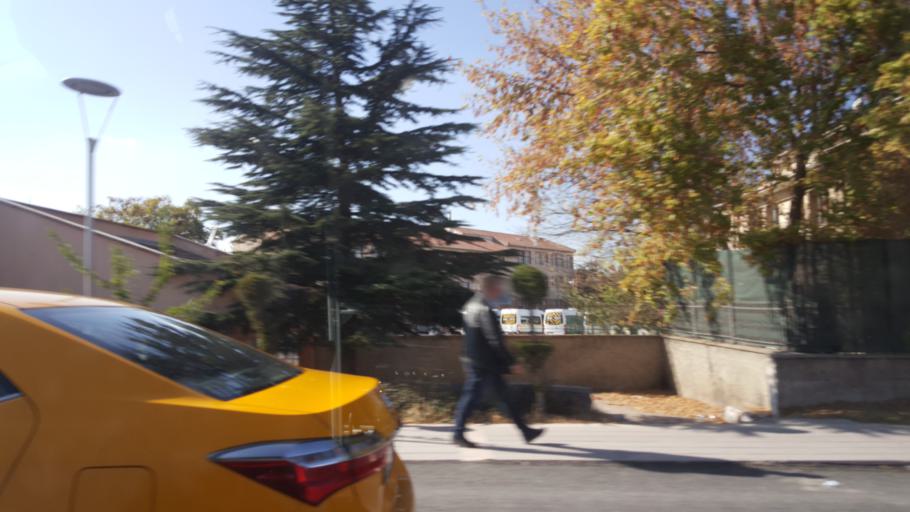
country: TR
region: Ankara
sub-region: Goelbasi
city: Golbasi
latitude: 39.7908
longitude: 32.8065
